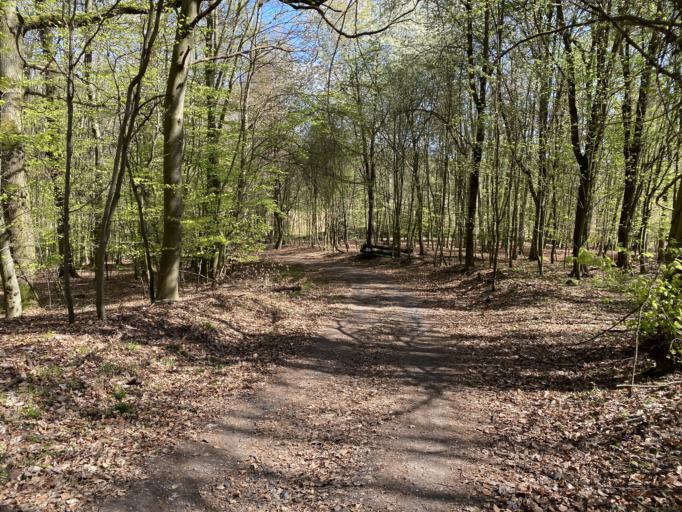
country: DE
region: Hesse
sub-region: Regierungsbezirk Darmstadt
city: Hammersbach
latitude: 50.2345
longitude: 9.0365
